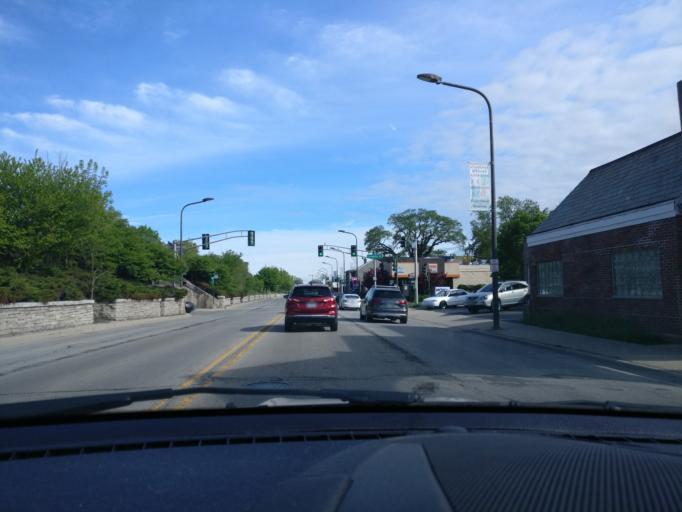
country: US
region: Illinois
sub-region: Cook County
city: Wilmette
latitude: 42.0667
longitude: -87.7008
